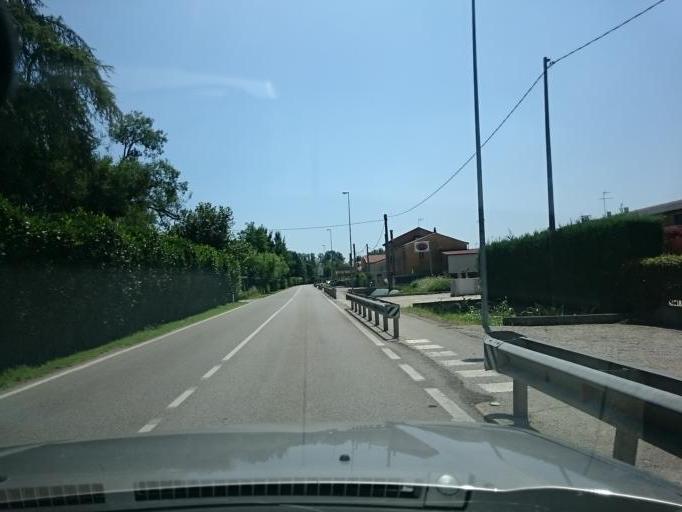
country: IT
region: Veneto
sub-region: Provincia di Padova
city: Villaguattera
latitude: 45.4368
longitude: 11.8243
